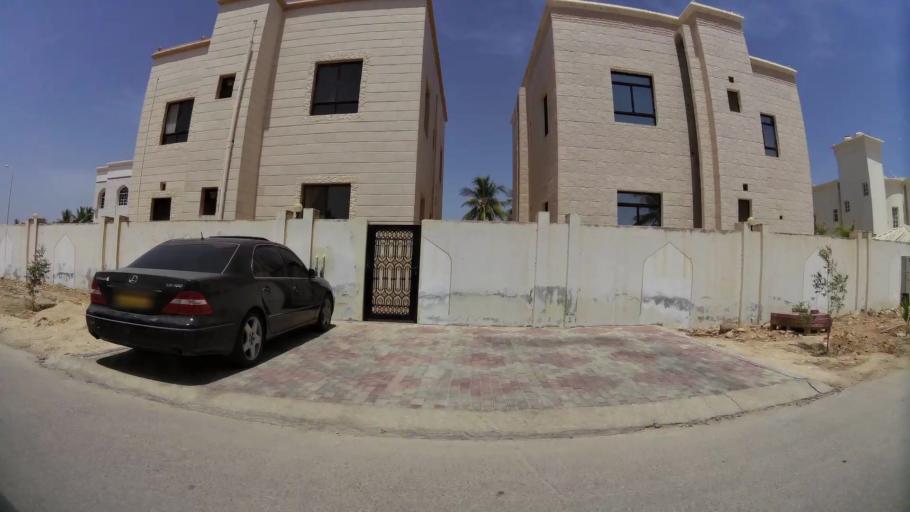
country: OM
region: Zufar
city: Salalah
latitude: 17.0645
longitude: 54.1509
